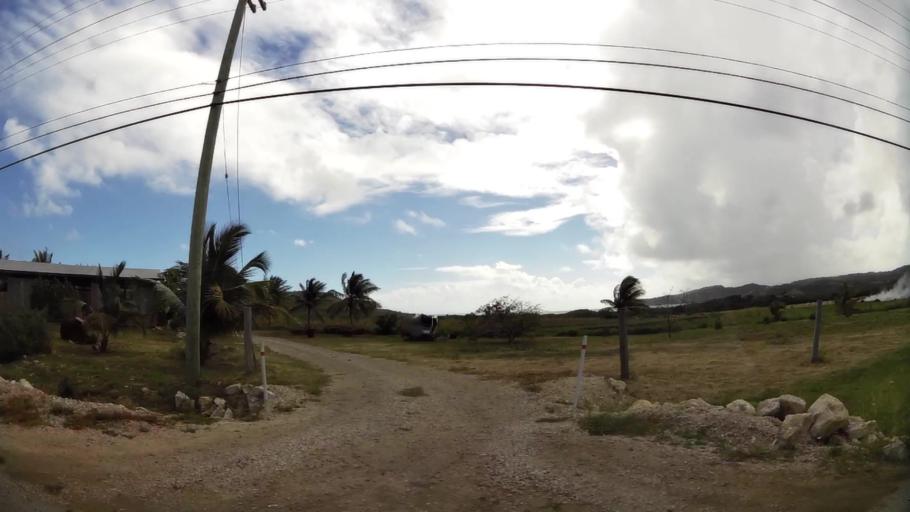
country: AG
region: Saint Paul
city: Liberta
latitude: 17.0543
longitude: -61.7415
